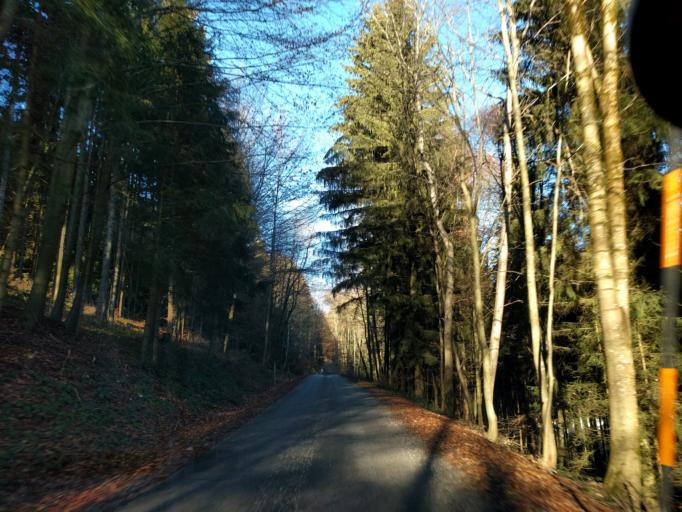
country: AT
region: Upper Austria
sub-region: Politischer Bezirk Urfahr-Umgebung
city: Kirchschlag bei Linz
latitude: 48.4124
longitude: 14.2892
